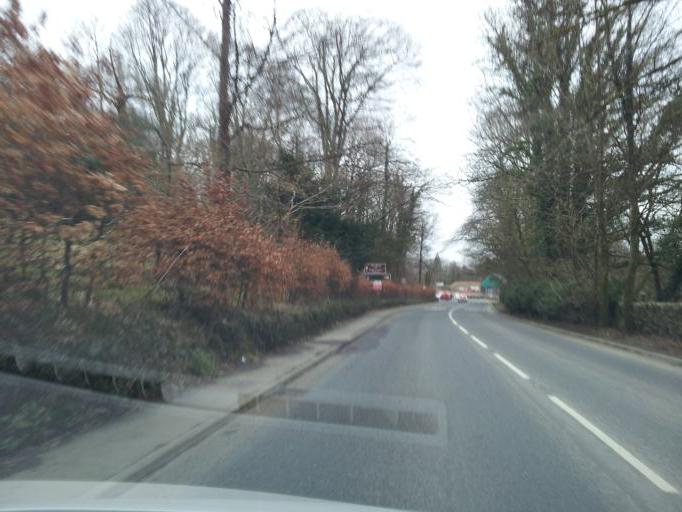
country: GB
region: England
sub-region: Cumbria
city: Windermere
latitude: 54.3717
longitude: -2.9199
